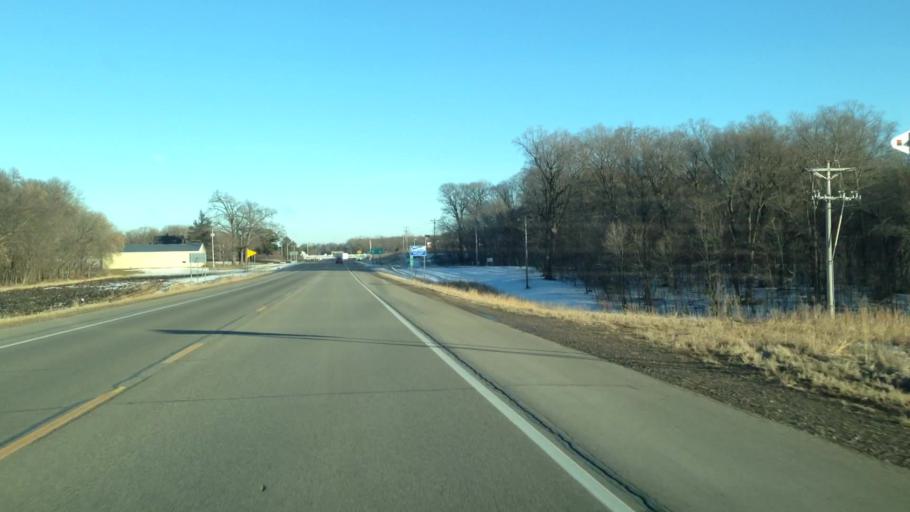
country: US
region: Minnesota
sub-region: Scott County
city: Elko New Market
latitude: 44.4715
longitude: -93.3012
